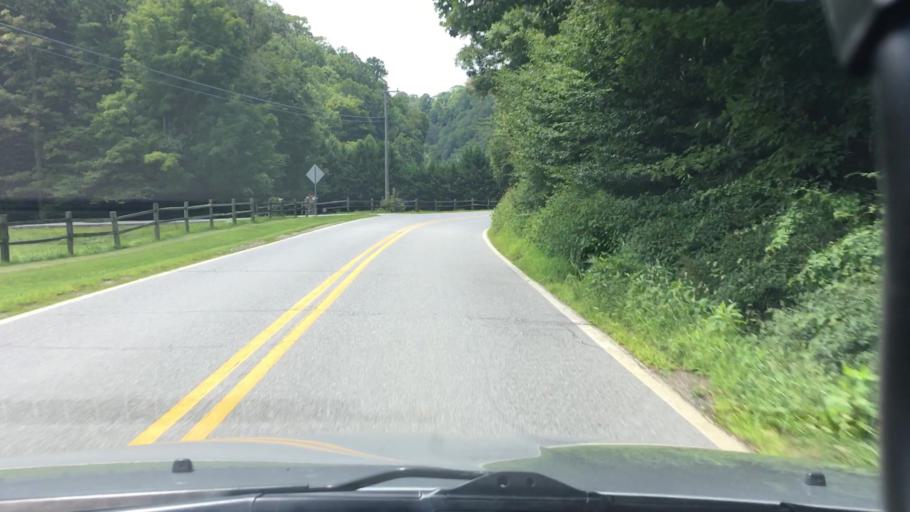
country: US
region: North Carolina
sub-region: Madison County
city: Mars Hill
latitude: 35.9191
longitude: -82.5404
